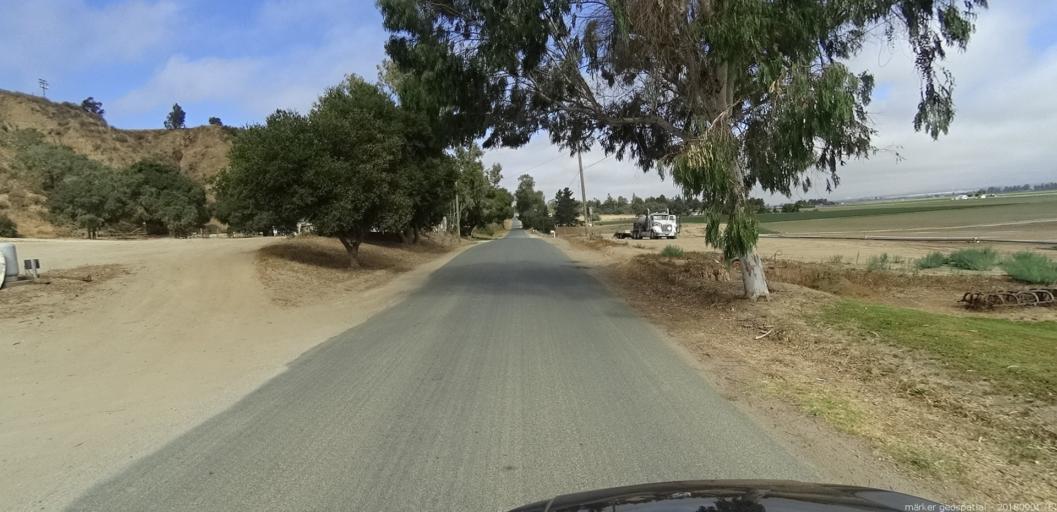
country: US
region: California
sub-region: Monterey County
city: Soledad
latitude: 36.3843
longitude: -121.3571
